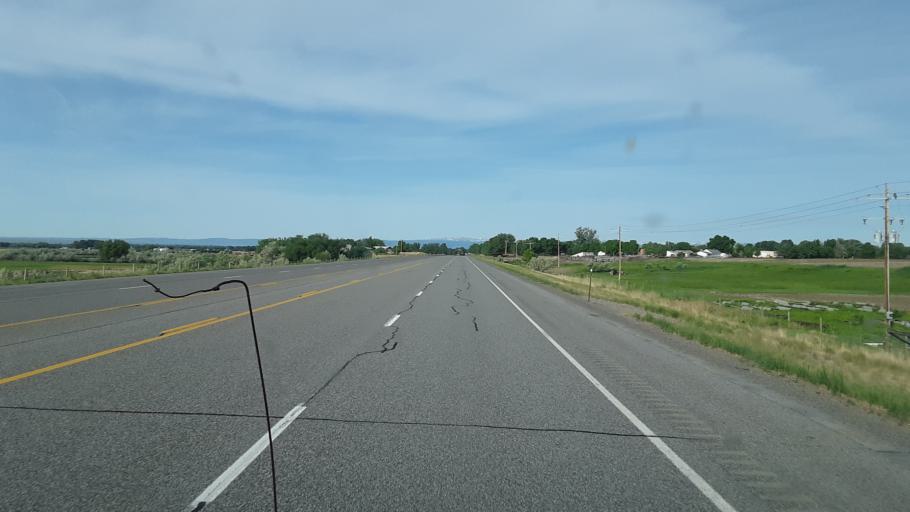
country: US
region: Wyoming
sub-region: Fremont County
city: Riverton
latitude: 43.1021
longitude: -108.3523
